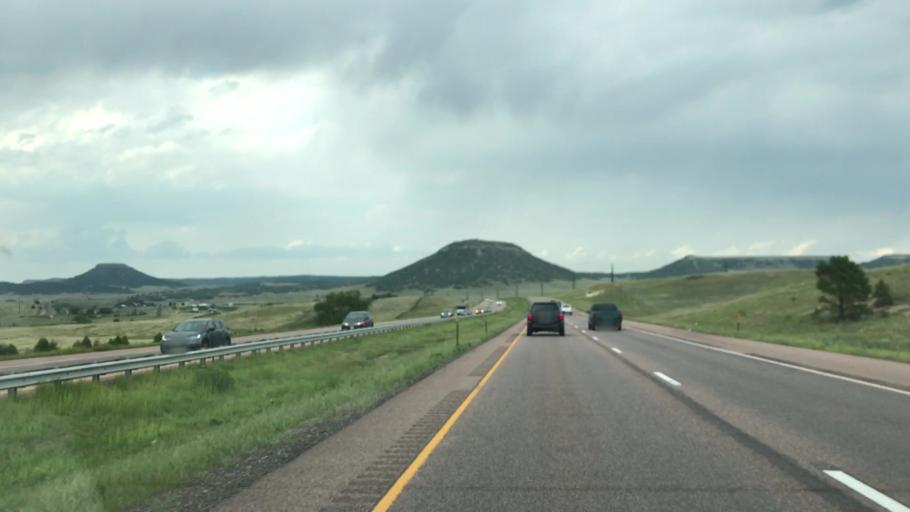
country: US
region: Colorado
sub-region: El Paso County
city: Woodmoor
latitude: 39.1672
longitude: -104.8524
